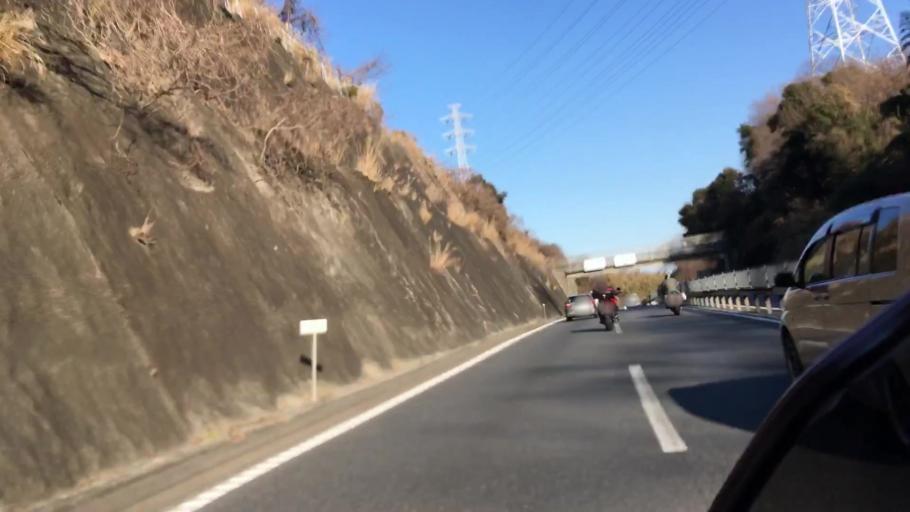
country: JP
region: Kanagawa
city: Oiso
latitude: 35.3268
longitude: 139.2849
